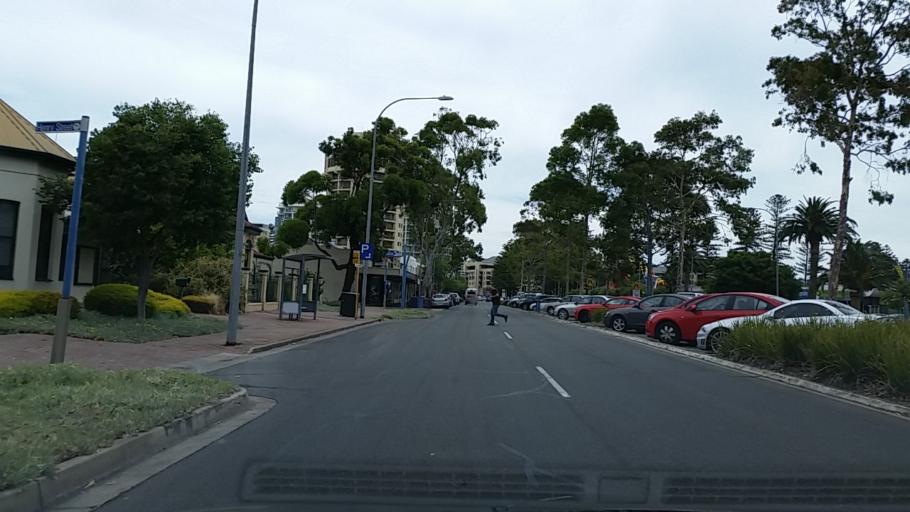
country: AU
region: South Australia
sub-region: Adelaide
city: Glenelg
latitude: -34.9766
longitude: 138.5163
